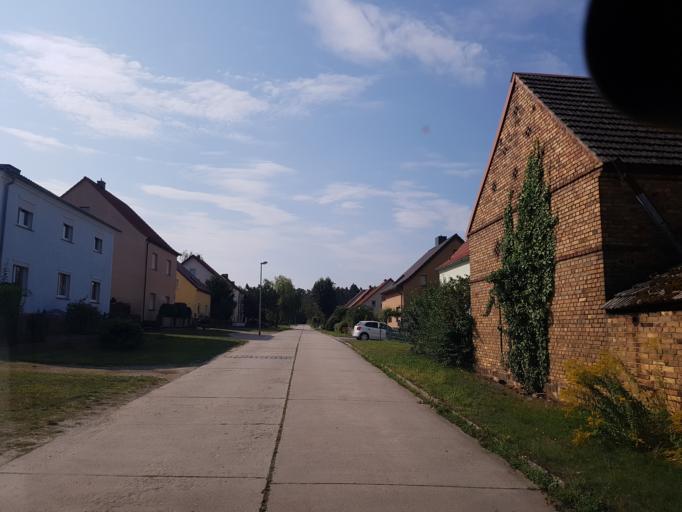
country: DE
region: Brandenburg
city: Plessa
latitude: 51.5323
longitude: 13.6660
